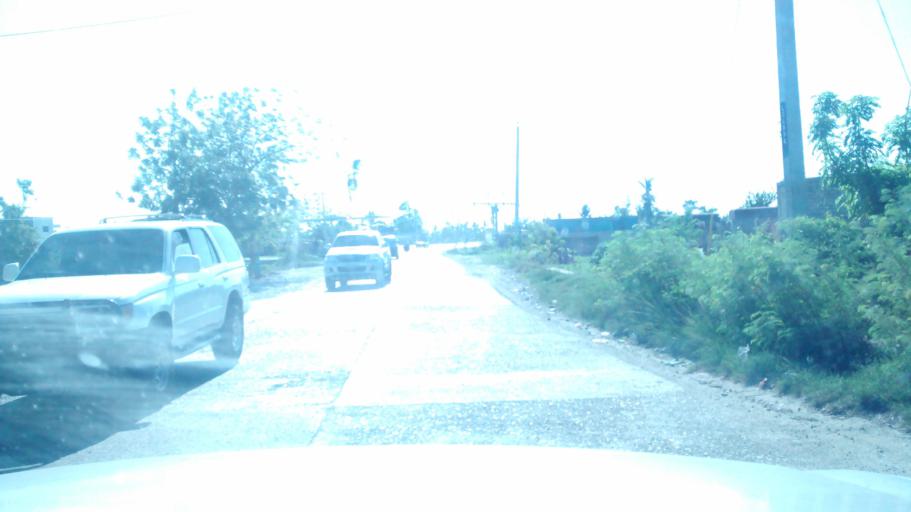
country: HT
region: Sud
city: Les Cayes
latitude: 18.2179
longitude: -73.7489
